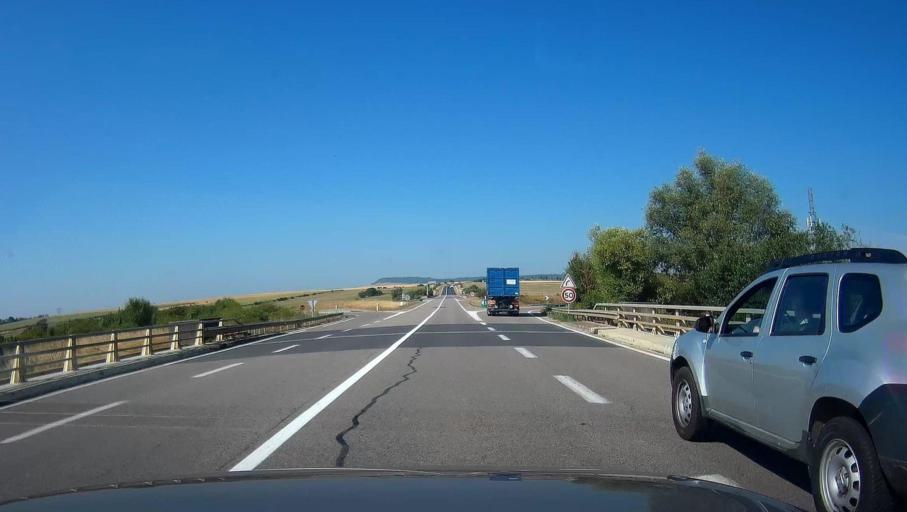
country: FR
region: Lorraine
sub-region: Departement de Meurthe-et-Moselle
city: Bainville-sur-Madon
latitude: 48.5825
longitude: 6.1056
